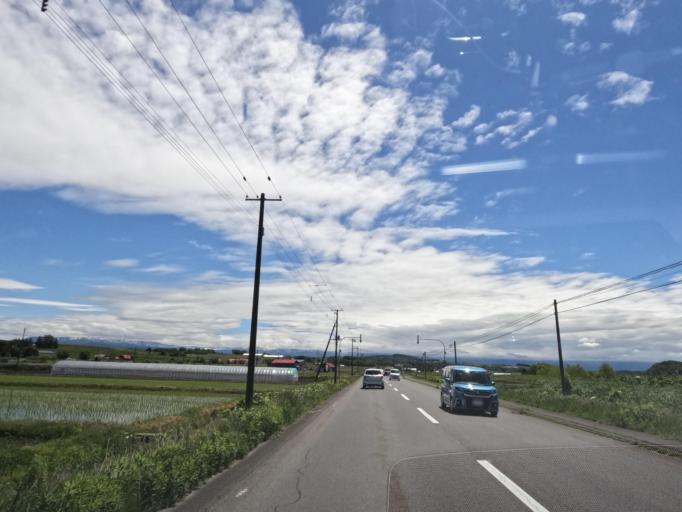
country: JP
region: Hokkaido
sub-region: Asahikawa-shi
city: Asahikawa
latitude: 43.6635
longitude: 142.4267
